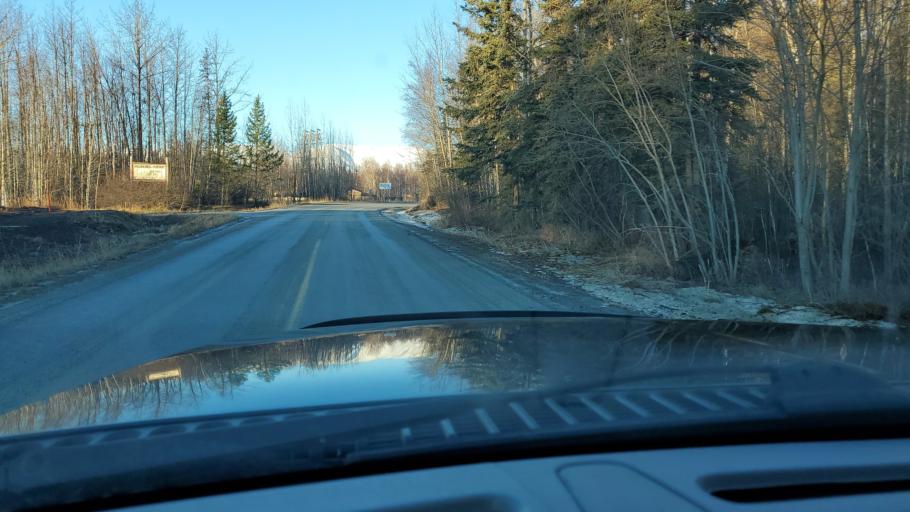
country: US
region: Alaska
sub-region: Matanuska-Susitna Borough
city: Gateway
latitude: 61.5908
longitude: -149.2451
